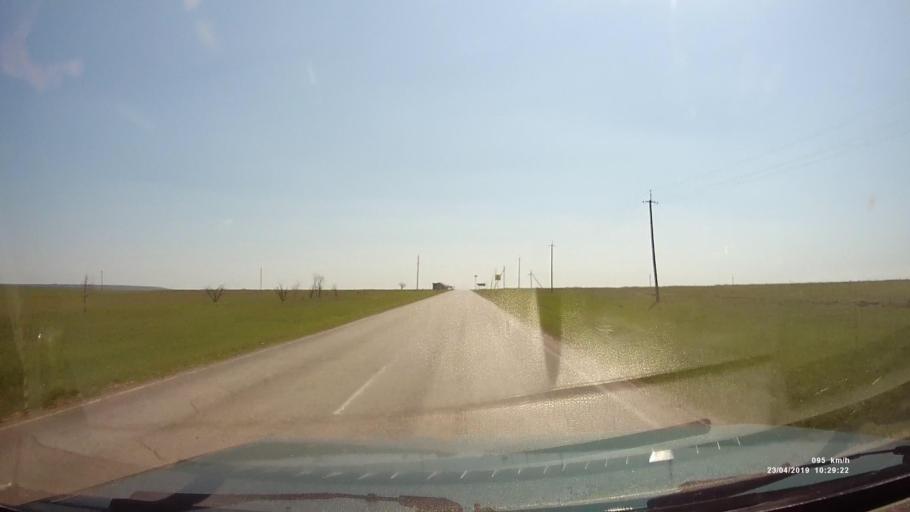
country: RU
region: Kalmykiya
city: Yashalta
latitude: 46.5990
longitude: 42.5252
